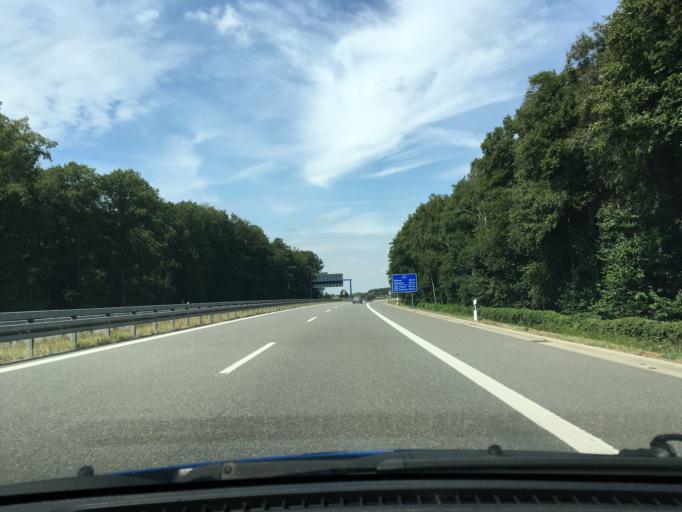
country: DE
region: Mecklenburg-Vorpommern
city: Mirow
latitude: 53.4321
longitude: 11.5121
